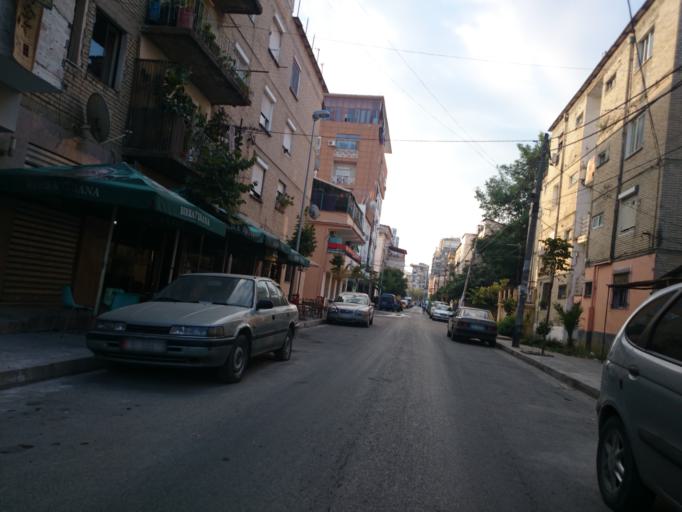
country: AL
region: Tirane
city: Tirana
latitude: 41.3265
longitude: 19.7937
